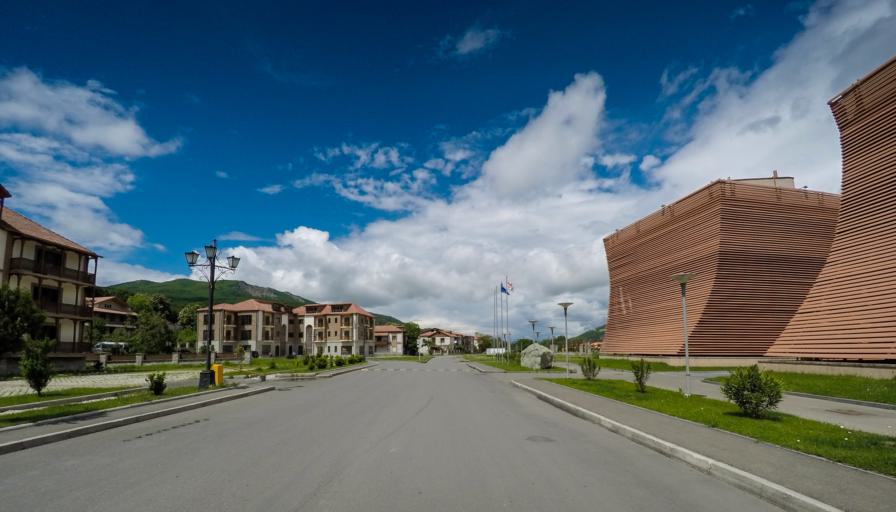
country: GE
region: Mtskheta-Mtianeti
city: Mtskheta
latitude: 41.8445
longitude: 44.7226
